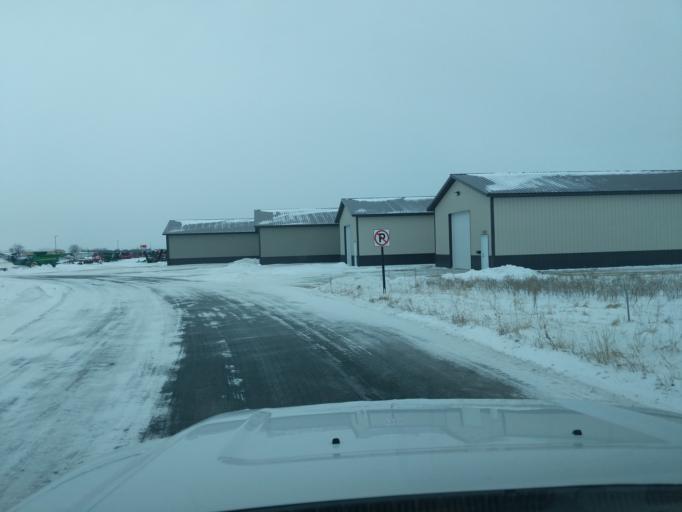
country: US
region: Minnesota
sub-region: Redwood County
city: Redwood Falls
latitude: 44.5423
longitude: -95.0780
